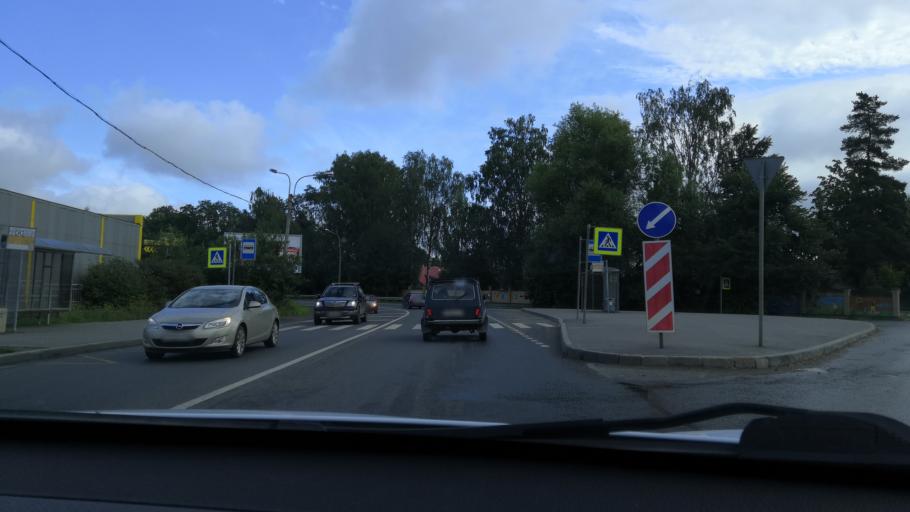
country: RU
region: St.-Petersburg
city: Tyarlevo
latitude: 59.6980
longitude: 30.4411
